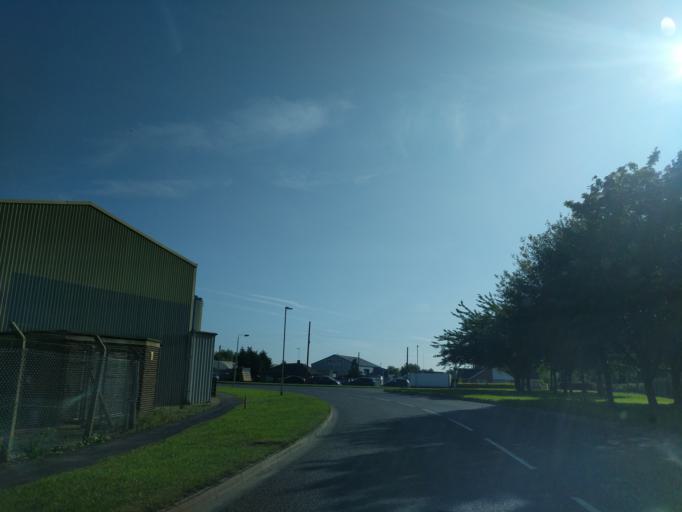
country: GB
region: England
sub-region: Lincolnshire
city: Bourne
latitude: 52.7604
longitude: -0.3636
